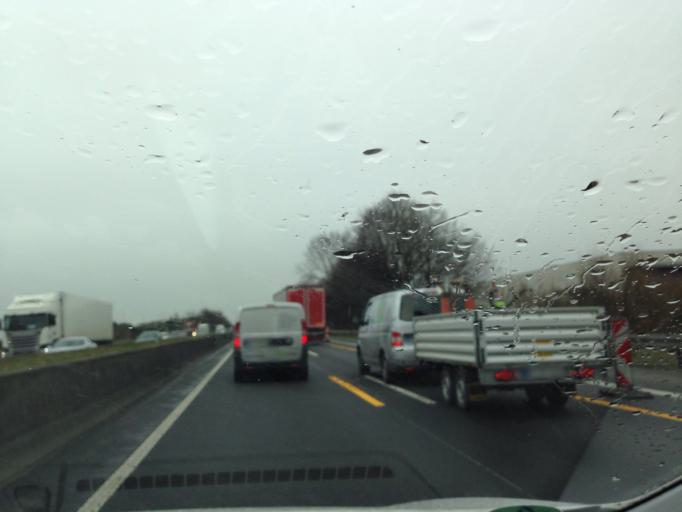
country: DE
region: North Rhine-Westphalia
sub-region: Regierungsbezirk Dusseldorf
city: Neubrueck
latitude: 51.1355
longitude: 6.6114
